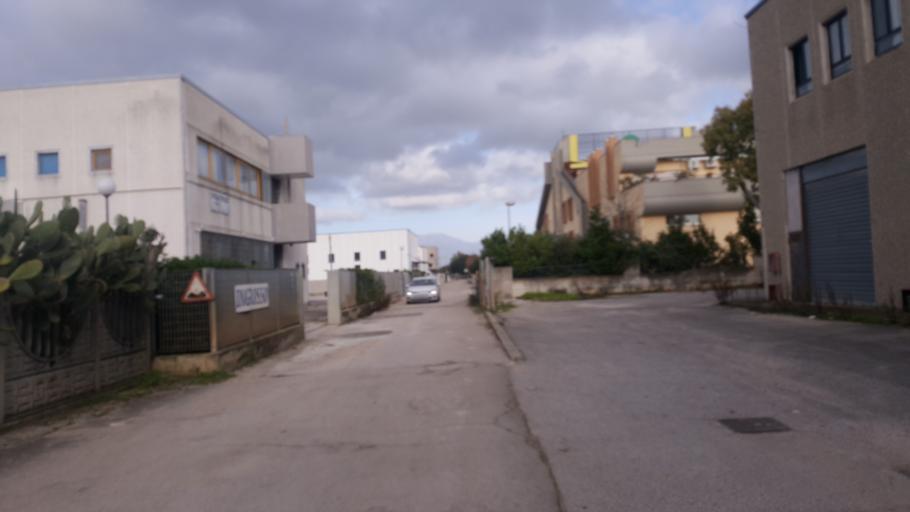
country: IT
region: Latium
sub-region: Provincia di Latina
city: Latina
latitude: 41.4746
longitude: 12.8849
